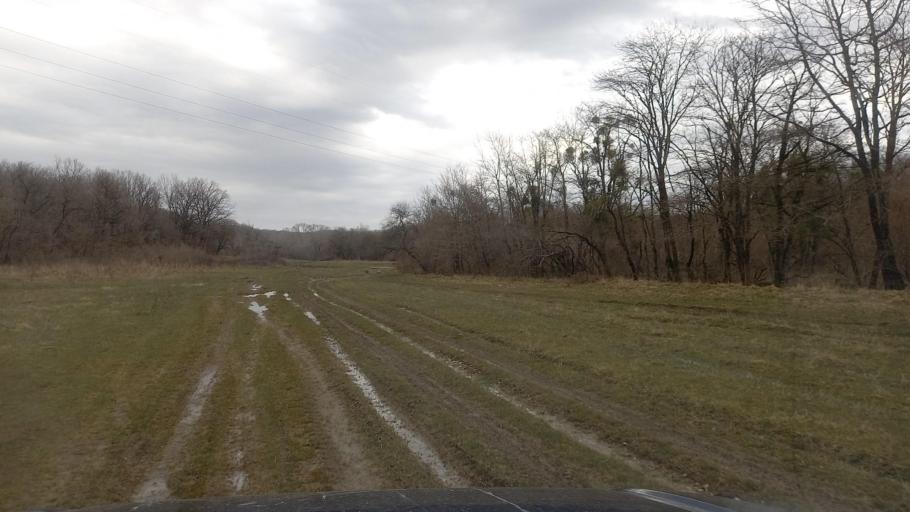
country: RU
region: Krasnodarskiy
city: Novorossiysk
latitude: 44.8534
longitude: 37.8401
